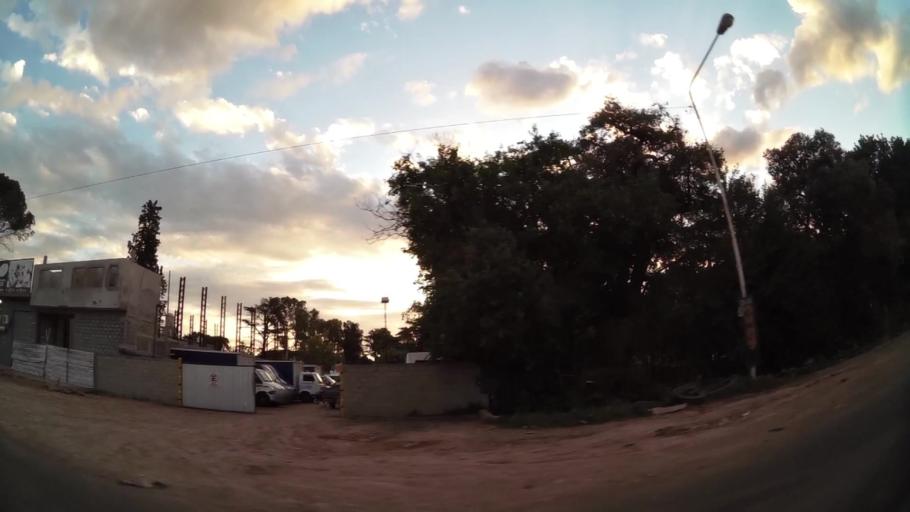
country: AR
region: Buenos Aires
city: Santa Catalina - Dique Lujan
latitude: -34.4852
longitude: -58.7751
